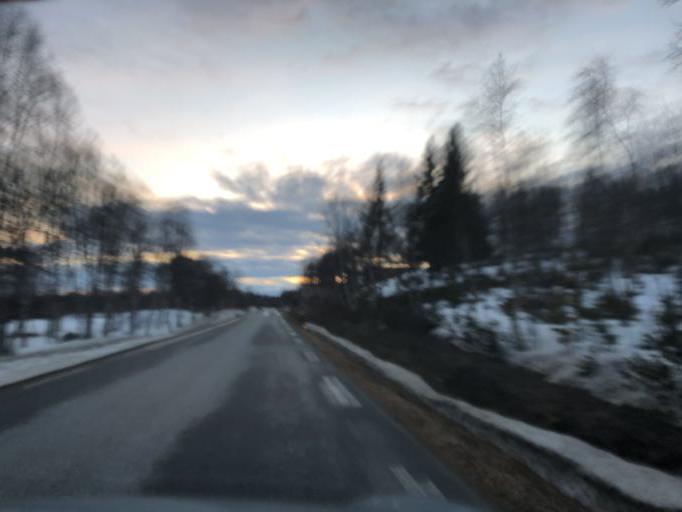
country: NO
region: Sor-Trondelag
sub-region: Tydal
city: Aas
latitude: 62.6730
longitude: 11.8135
